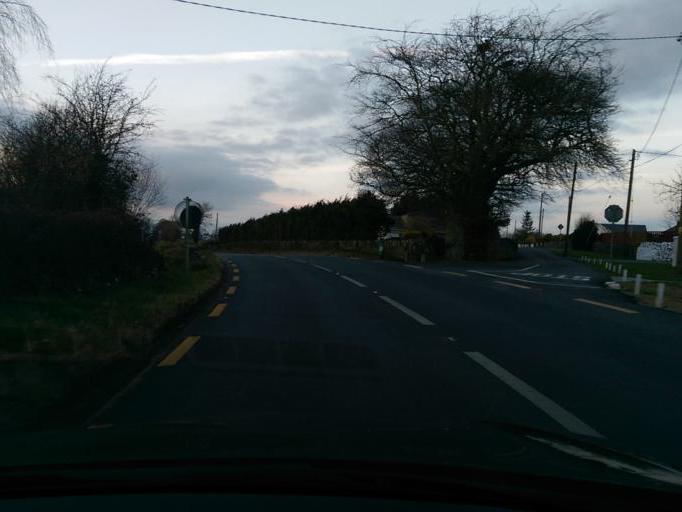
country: IE
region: Munster
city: Nenagh Bridge
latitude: 52.9806
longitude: -8.1305
